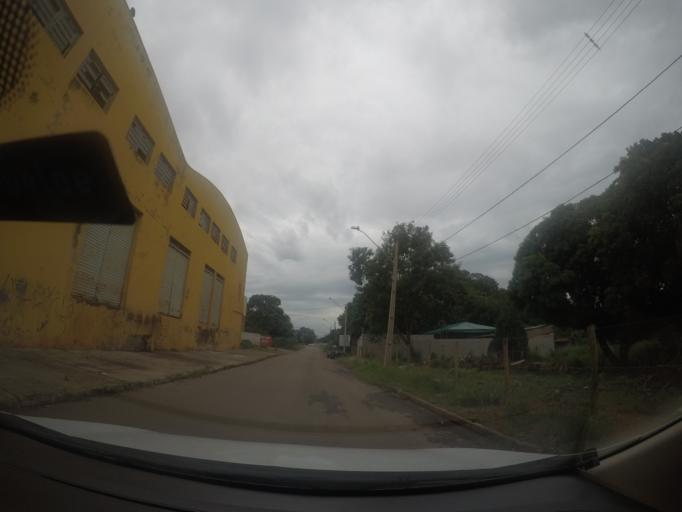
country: BR
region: Goias
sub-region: Goiania
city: Goiania
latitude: -16.6646
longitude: -49.3133
